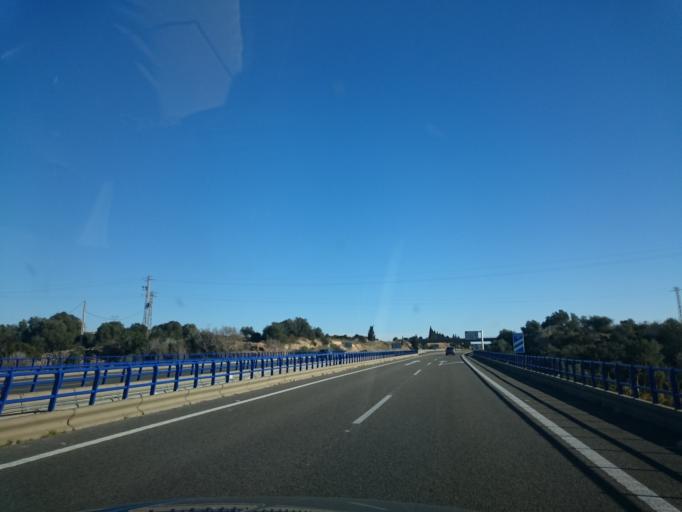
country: ES
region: Catalonia
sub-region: Provincia de Tarragona
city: Amposta
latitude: 40.7289
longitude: 0.5754
